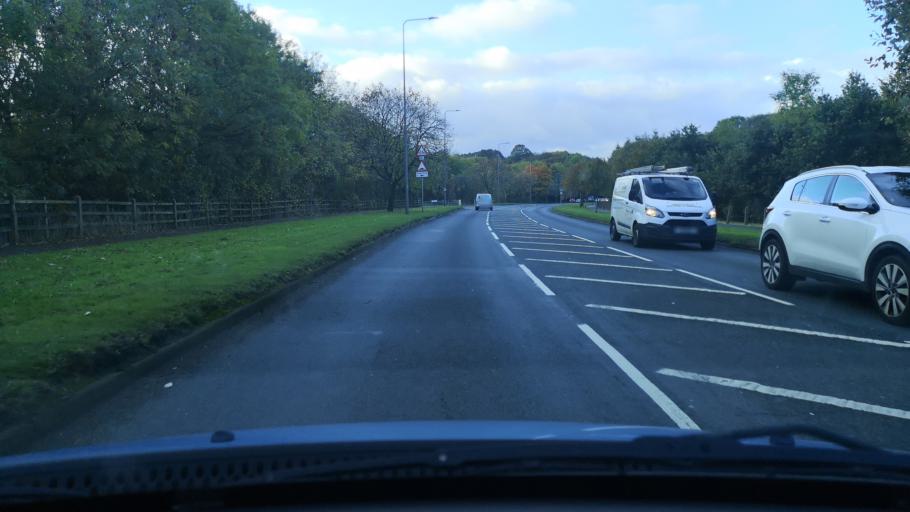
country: GB
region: England
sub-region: North Lincolnshire
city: Scunthorpe
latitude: 53.5802
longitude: -0.6678
